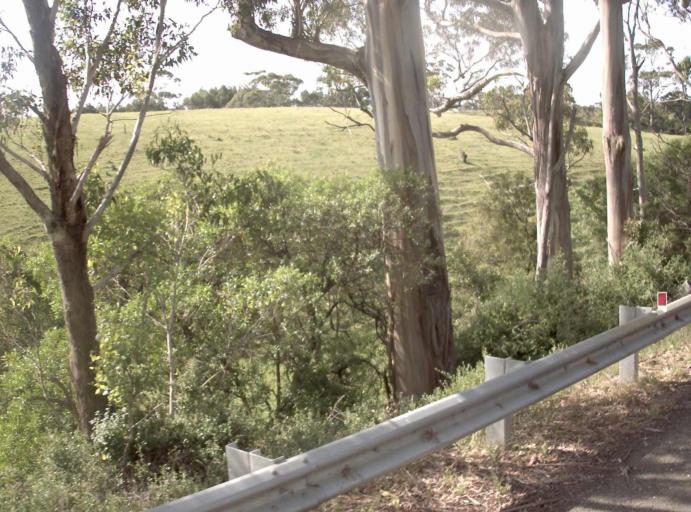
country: AU
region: Victoria
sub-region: East Gippsland
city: Lakes Entrance
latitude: -37.8556
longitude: 148.0307
